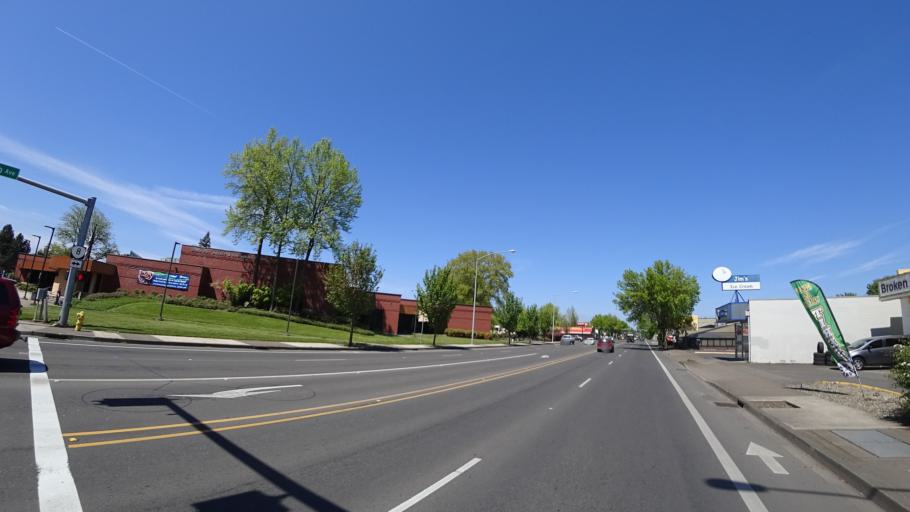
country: US
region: Oregon
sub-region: Washington County
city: Hillsboro
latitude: 45.5150
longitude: -122.9739
